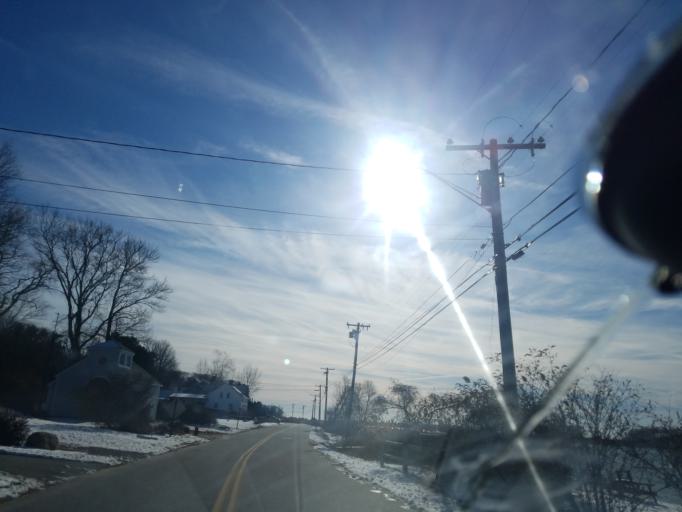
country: US
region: Connecticut
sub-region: New London County
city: Niantic
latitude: 41.3053
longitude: -72.2176
